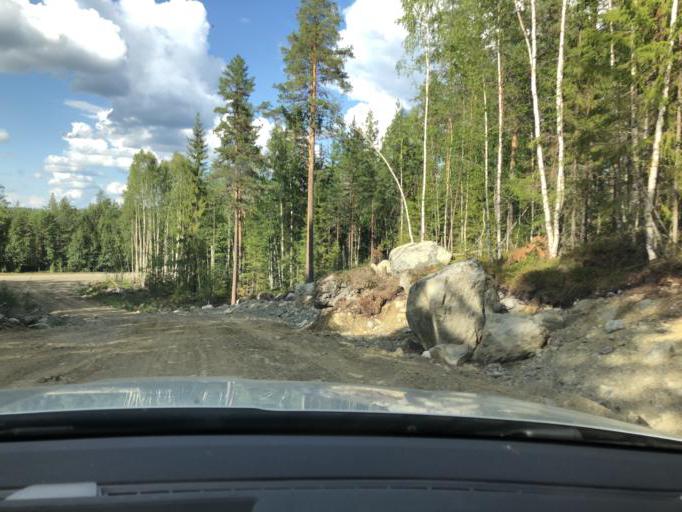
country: SE
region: Vaesternorrland
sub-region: Solleftea Kommun
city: Solleftea
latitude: 63.3123
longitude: 17.2806
